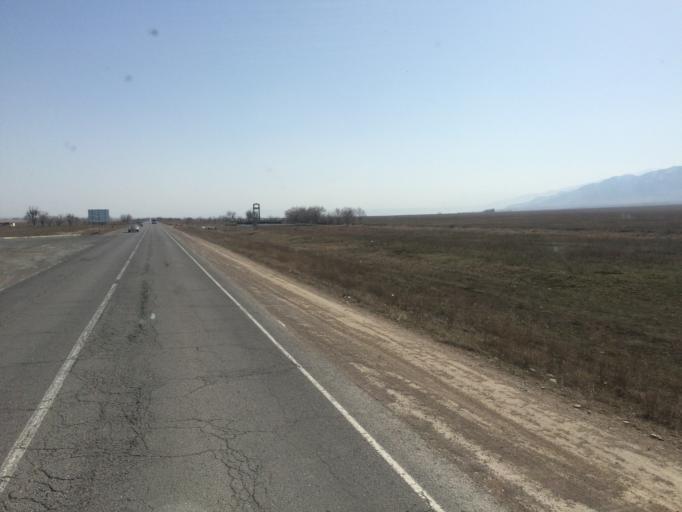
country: KG
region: Chuy
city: Ivanovka
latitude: 43.3711
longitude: 75.2922
